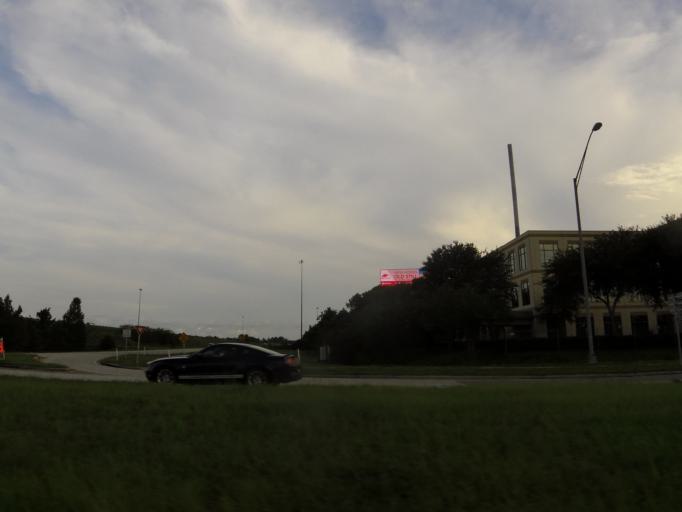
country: US
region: Florida
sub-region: Saint Johns County
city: Ponte Vedra Beach
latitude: 30.2360
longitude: -81.5154
